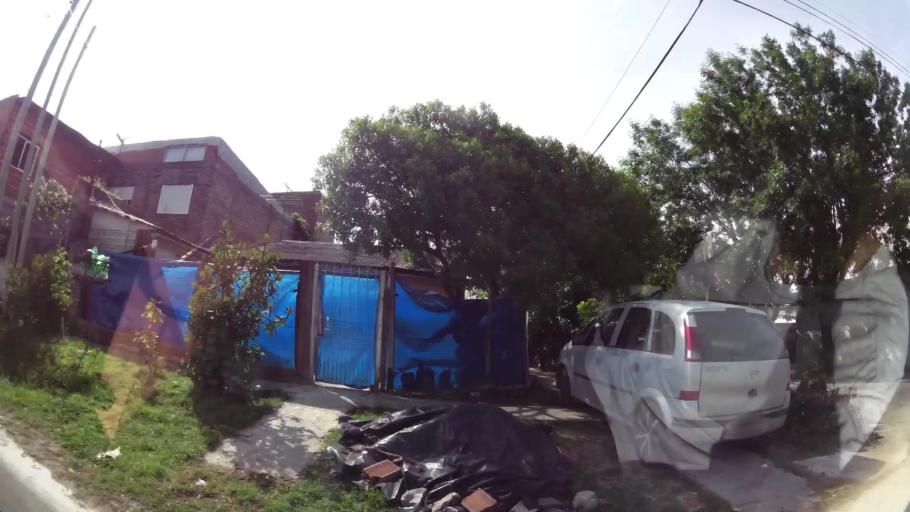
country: AR
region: Buenos Aires
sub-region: Partido de Quilmes
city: Quilmes
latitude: -34.7644
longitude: -58.2409
